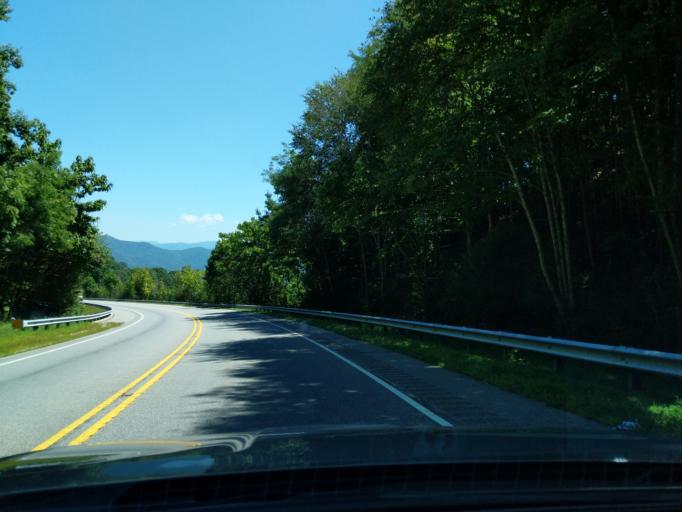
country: US
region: North Carolina
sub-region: Macon County
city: Franklin
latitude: 35.1297
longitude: -83.5315
